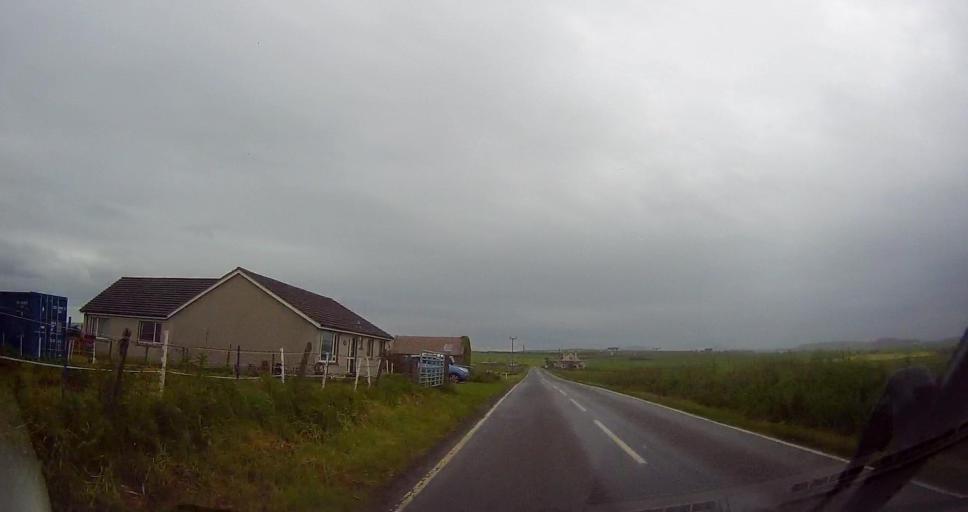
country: GB
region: Scotland
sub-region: Orkney Islands
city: Stromness
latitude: 59.0406
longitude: -3.2821
